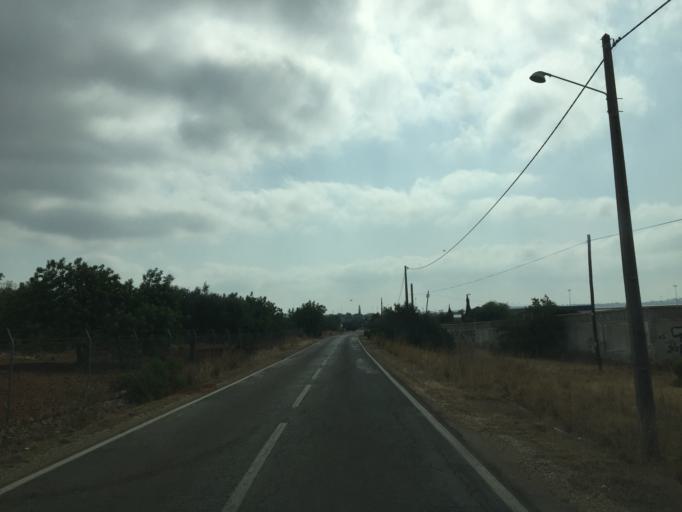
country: PT
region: Faro
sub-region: Faro
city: Santa Barbara de Nexe
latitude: 37.0904
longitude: -7.9297
